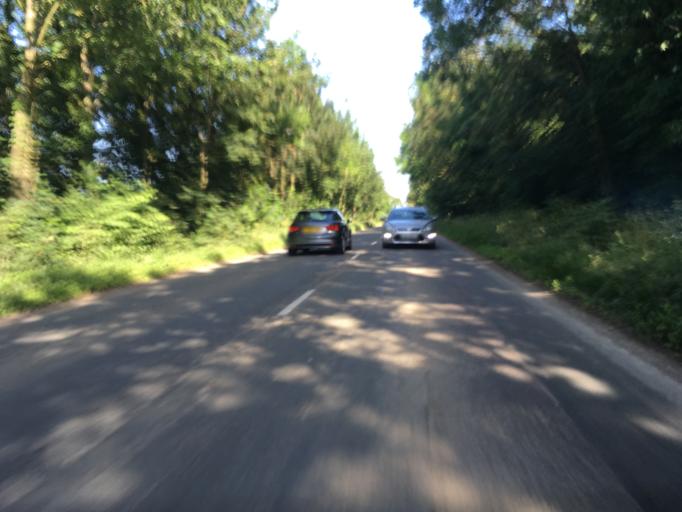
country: GB
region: England
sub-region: Oxfordshire
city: Bicester
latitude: 51.9029
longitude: -1.1921
